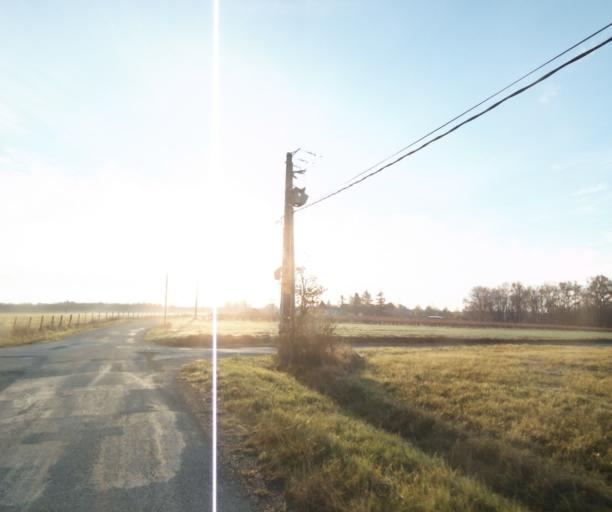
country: FR
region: Poitou-Charentes
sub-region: Departement de la Charente-Maritime
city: Fontcouverte
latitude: 45.7658
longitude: -0.5586
